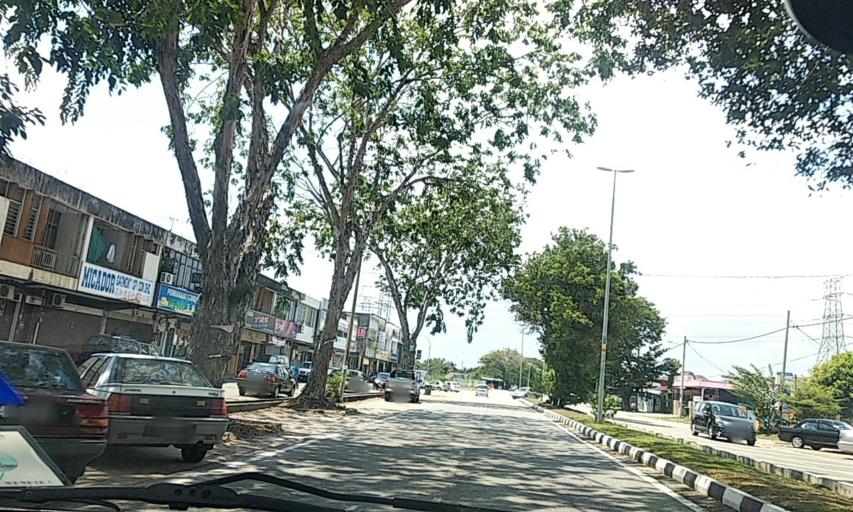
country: MY
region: Kedah
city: Sungai Petani
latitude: 5.6361
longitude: 100.4740
